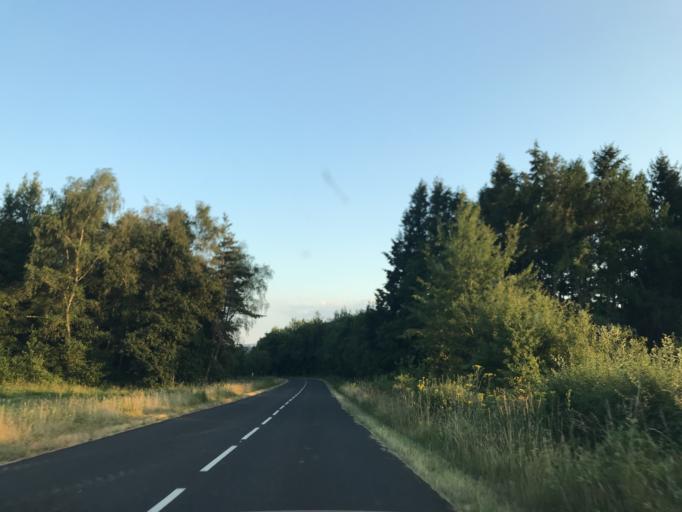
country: FR
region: Auvergne
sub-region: Departement du Puy-de-Dome
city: Courpiere
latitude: 45.7514
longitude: 3.6040
